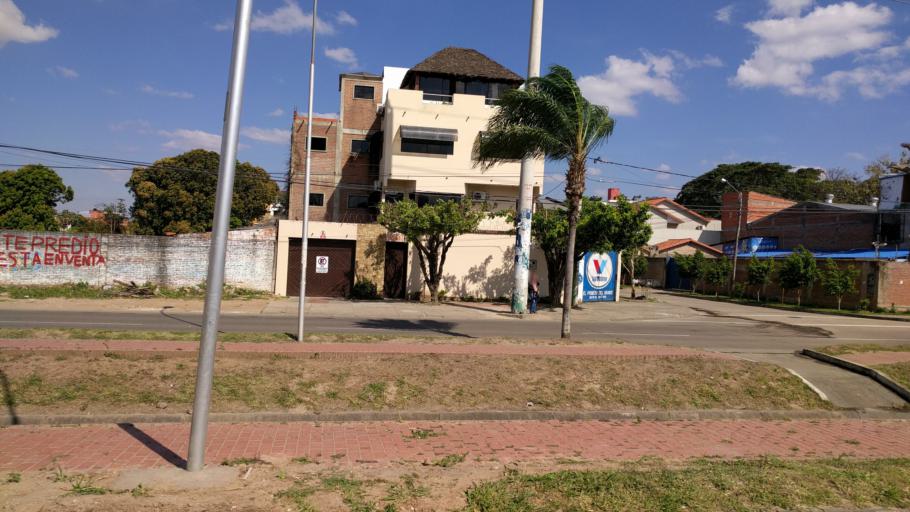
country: BO
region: Santa Cruz
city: Santa Cruz de la Sierra
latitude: -17.7858
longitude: -63.2146
